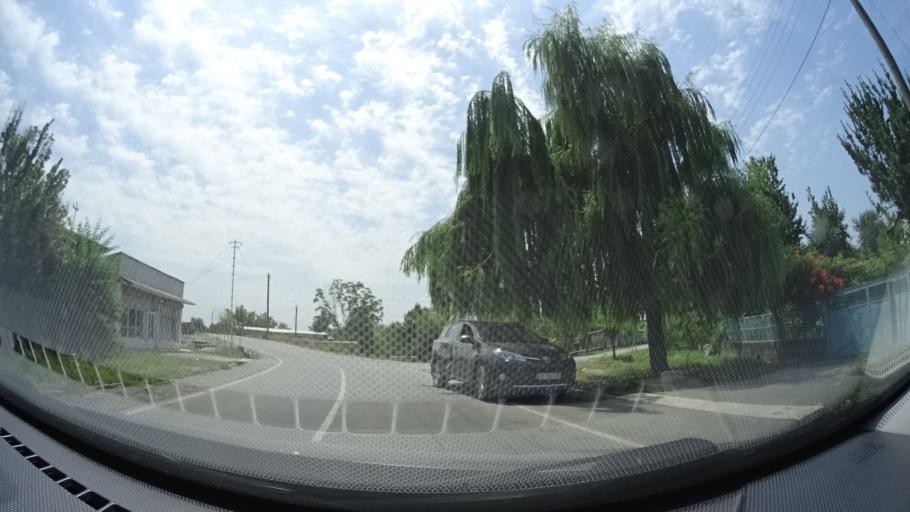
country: GE
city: Bagdadi
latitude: 41.8129
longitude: 46.1405
